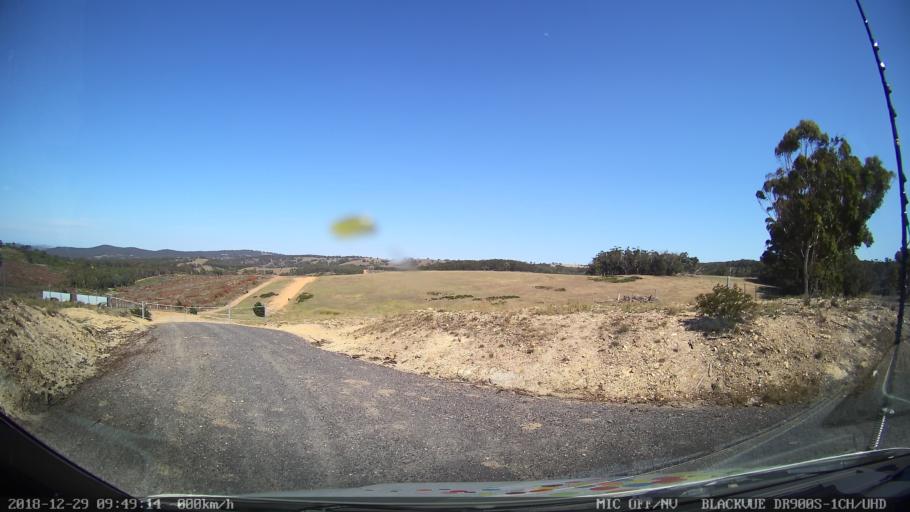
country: AU
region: New South Wales
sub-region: Upper Lachlan Shire
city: Crookwell
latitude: -34.7174
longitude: 149.4562
